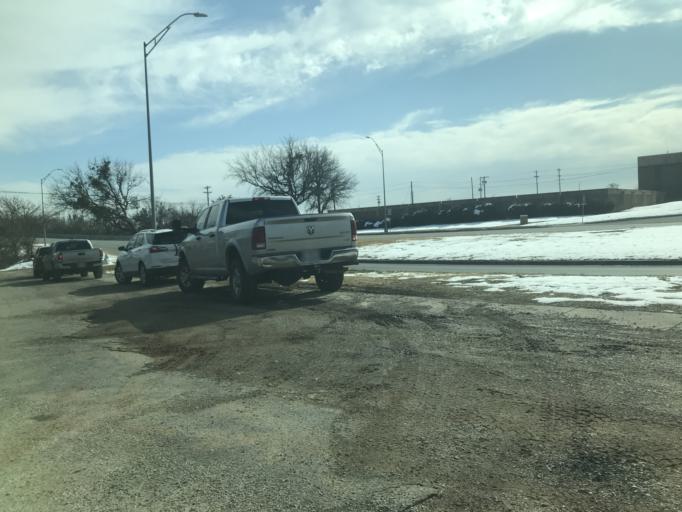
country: US
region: Texas
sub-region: Taylor County
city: Abilene
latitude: 32.4504
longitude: -99.7255
